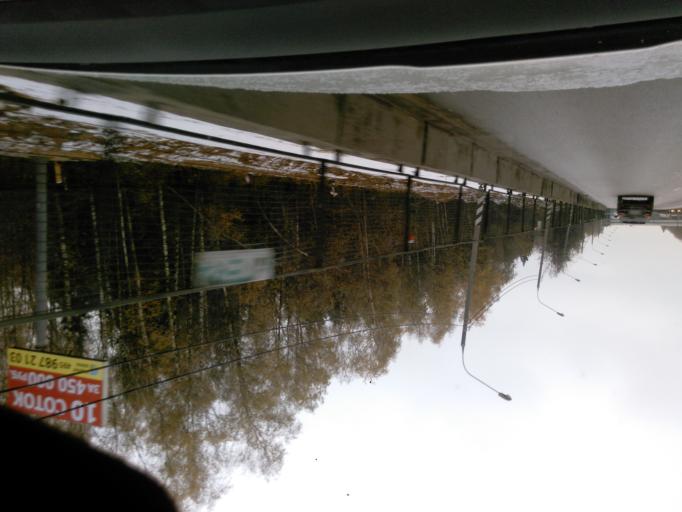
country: RU
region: Moskovskaya
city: Mendeleyevo
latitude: 56.0114
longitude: 37.2150
